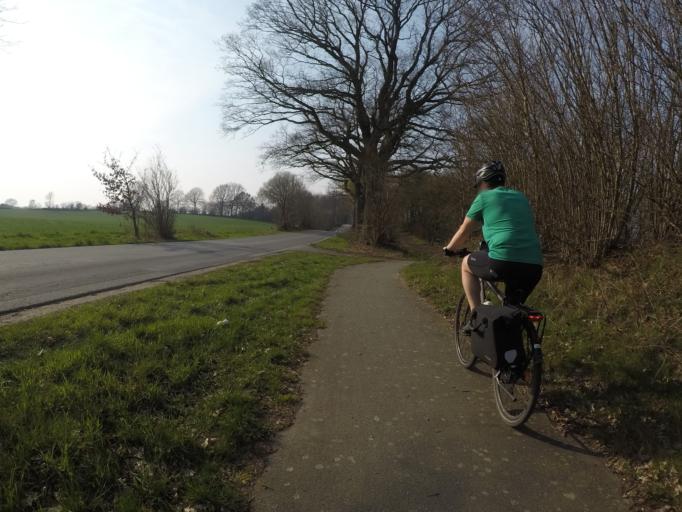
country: DE
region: Schleswig-Holstein
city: Kukels
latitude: 53.9108
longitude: 10.2293
